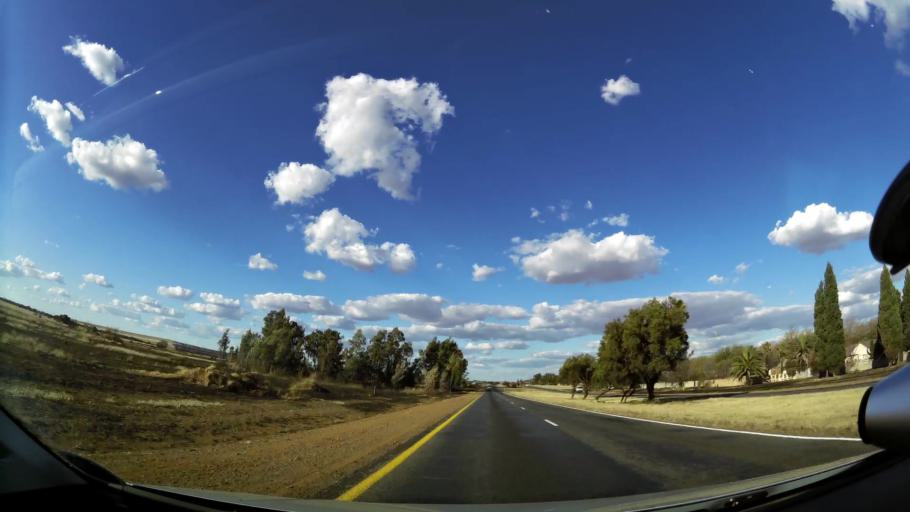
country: ZA
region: North-West
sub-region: Dr Kenneth Kaunda District Municipality
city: Stilfontein
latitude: -26.8412
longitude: 26.7528
